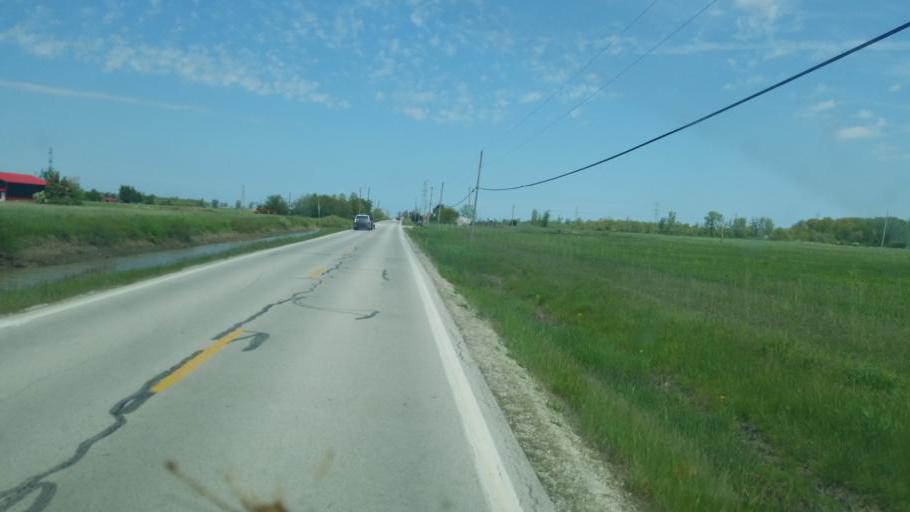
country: US
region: Ohio
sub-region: Ottawa County
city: Oak Harbor
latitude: 41.5837
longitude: -83.1450
